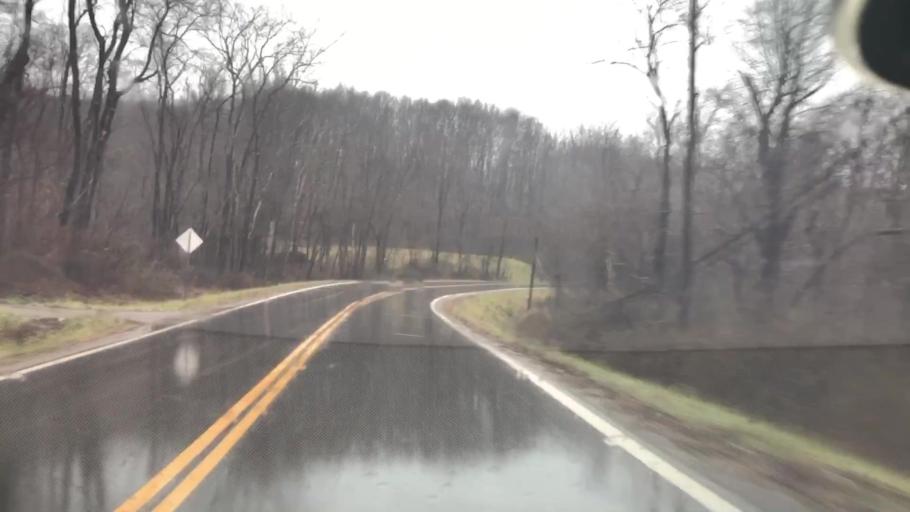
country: US
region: Ohio
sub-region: Harrison County
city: Cadiz
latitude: 40.3603
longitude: -81.0292
